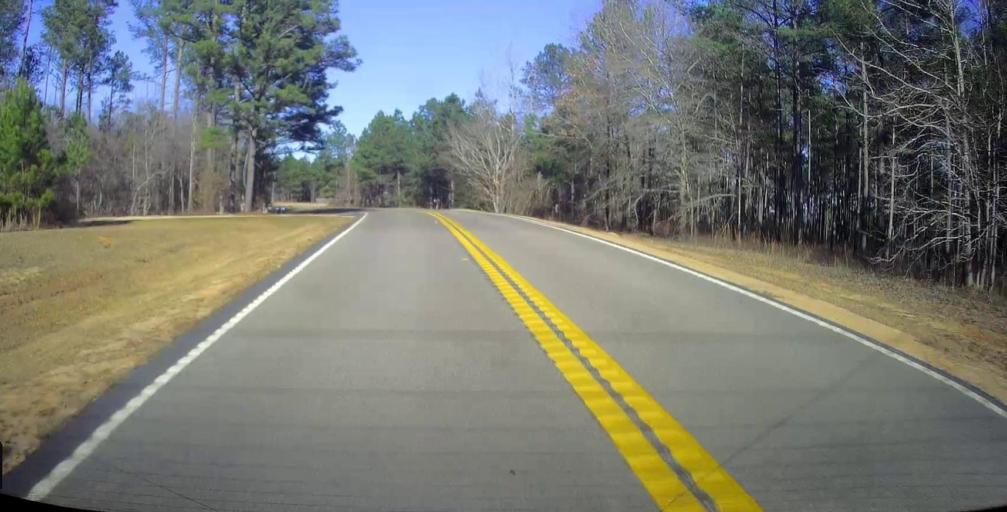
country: US
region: Georgia
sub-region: Taylor County
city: Butler
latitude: 32.6550
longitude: -84.3658
